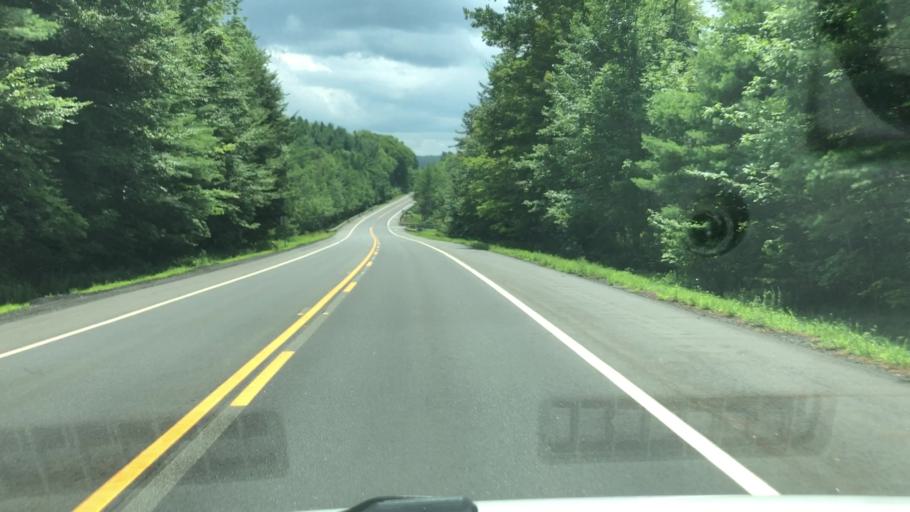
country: US
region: Massachusetts
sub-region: Franklin County
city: Ashfield
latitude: 42.4814
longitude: -72.8103
